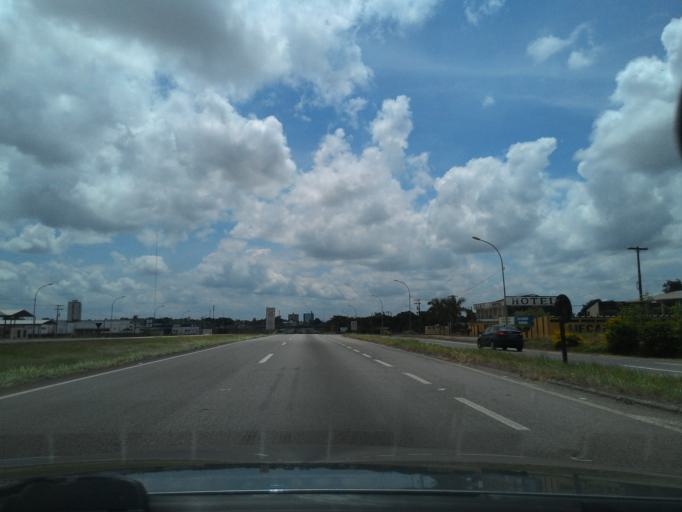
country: BR
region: Sao Paulo
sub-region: Registro
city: Registro
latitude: -24.5152
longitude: -47.8514
